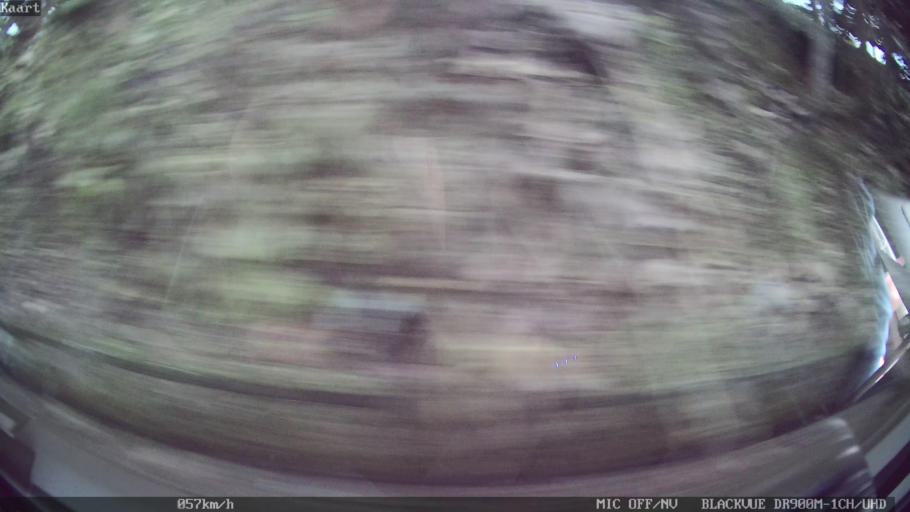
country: ID
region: Bali
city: Penebel
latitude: -8.4150
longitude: 115.1448
